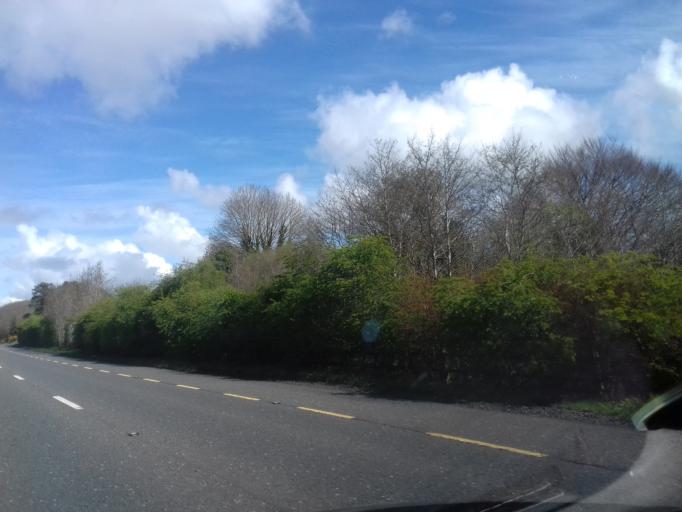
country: IE
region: Ulster
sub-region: An Cabhan
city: Cavan
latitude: 54.0560
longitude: -7.3868
